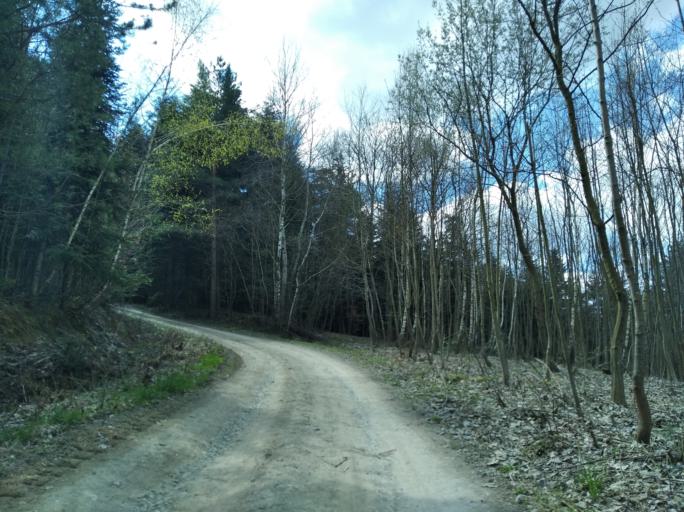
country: PL
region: Subcarpathian Voivodeship
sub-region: Powiat strzyzowski
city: Wysoka Strzyzowska
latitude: 49.8326
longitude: 21.7676
